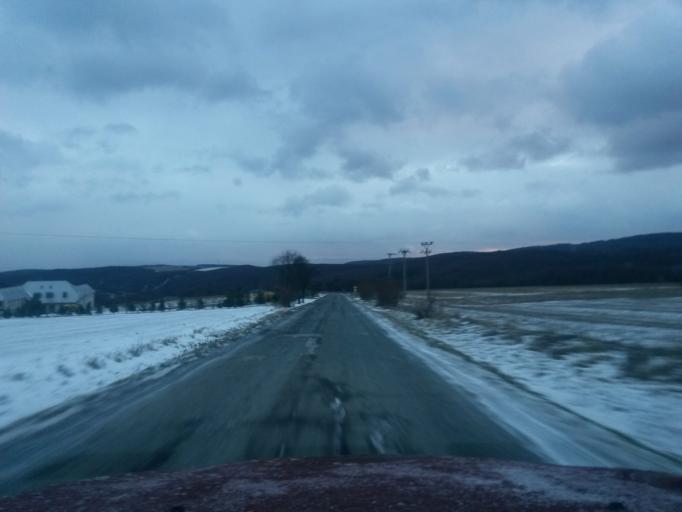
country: SK
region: Kosicky
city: Kosice
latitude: 48.7395
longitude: 21.1220
